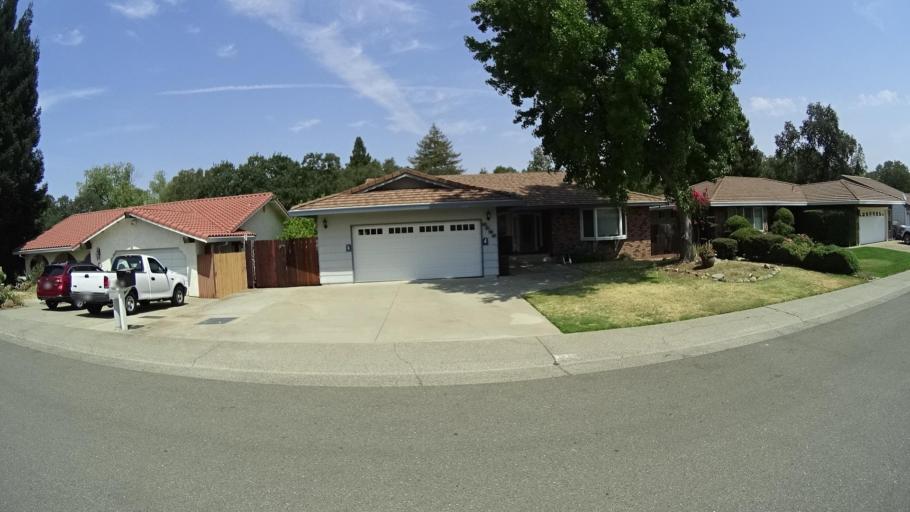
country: US
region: California
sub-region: Placer County
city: Rocklin
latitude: 38.7983
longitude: -121.2368
